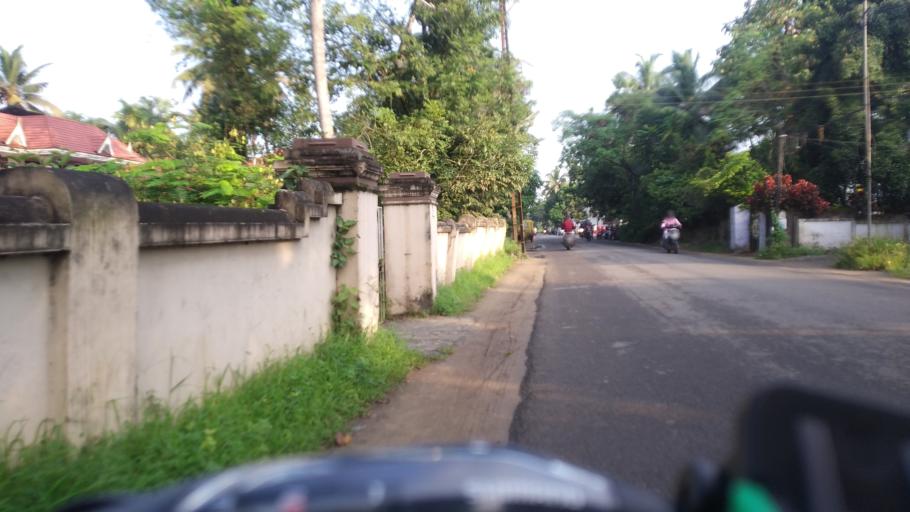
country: IN
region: Kerala
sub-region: Ernakulam
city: Elur
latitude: 10.0737
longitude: 76.2117
